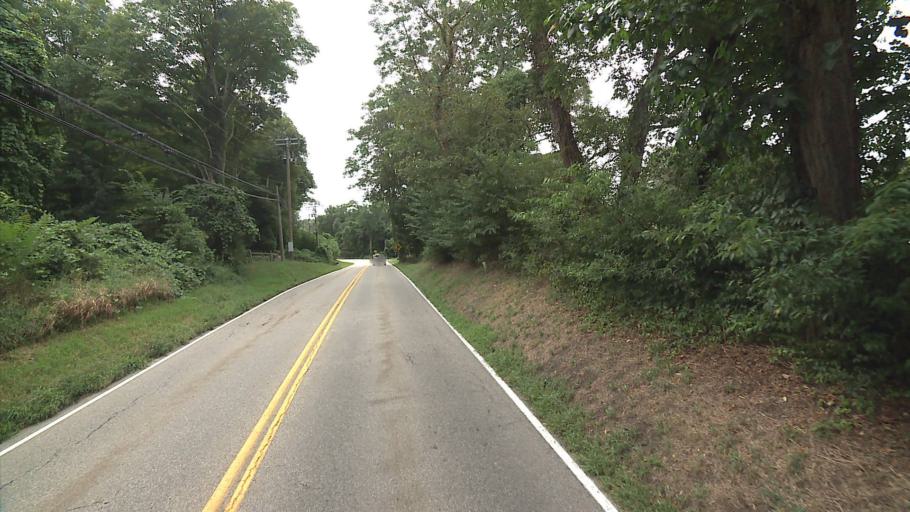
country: US
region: Connecticut
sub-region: Middlesex County
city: Essex Village
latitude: 41.3690
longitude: -72.3462
